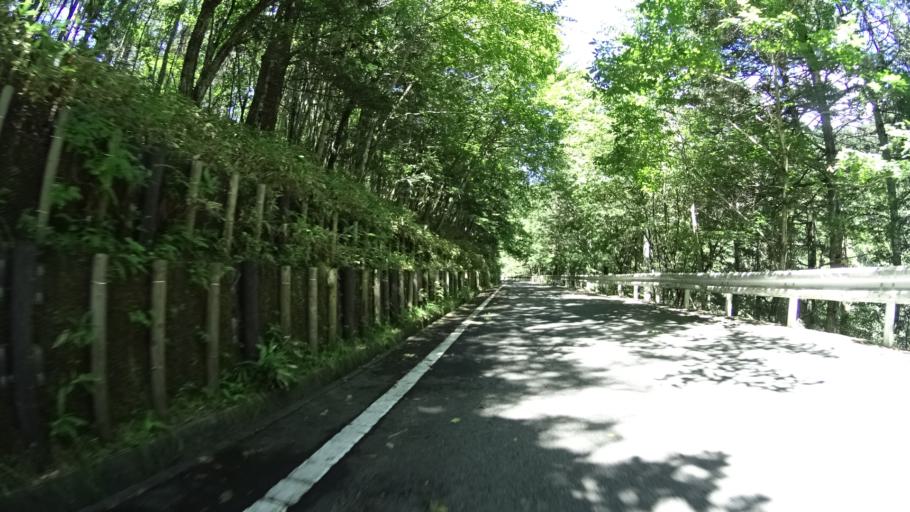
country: JP
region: Yamanashi
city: Enzan
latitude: 35.7323
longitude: 138.8357
